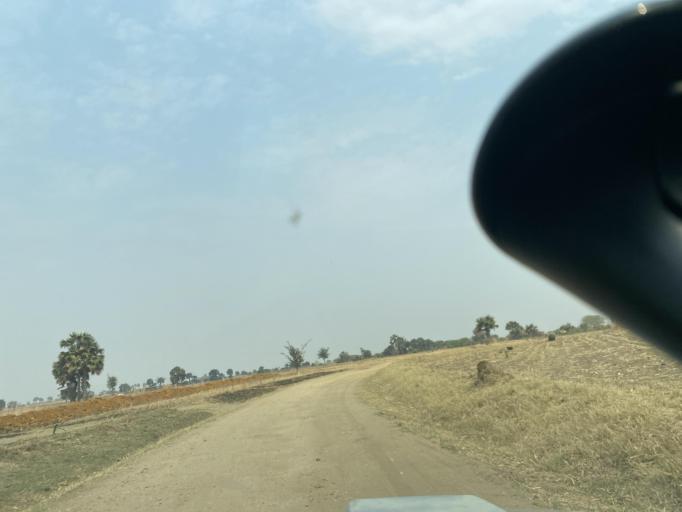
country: ZM
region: Lusaka
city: Kafue
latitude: -15.6471
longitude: 28.0761
